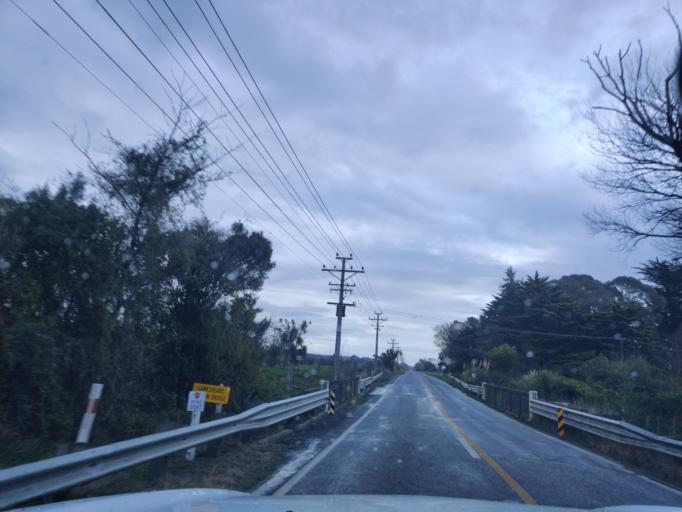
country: NZ
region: Manawatu-Wanganui
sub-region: Palmerston North City
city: Palmerston North
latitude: -40.3440
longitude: 175.7113
